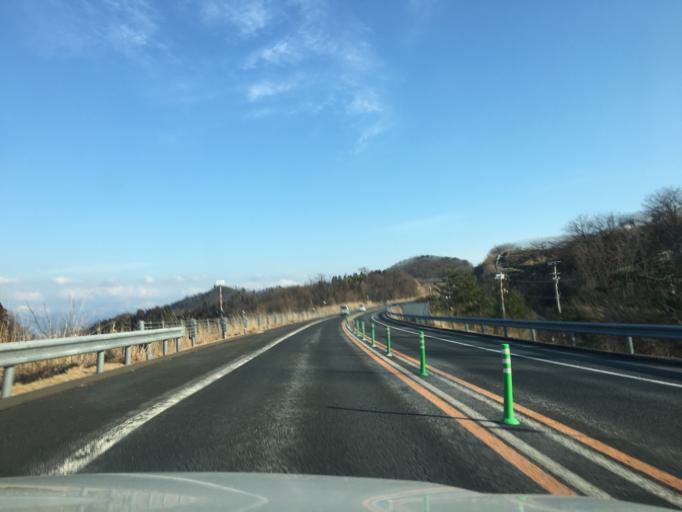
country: JP
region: Yamagata
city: Sagae
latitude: 38.4003
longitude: 140.2083
